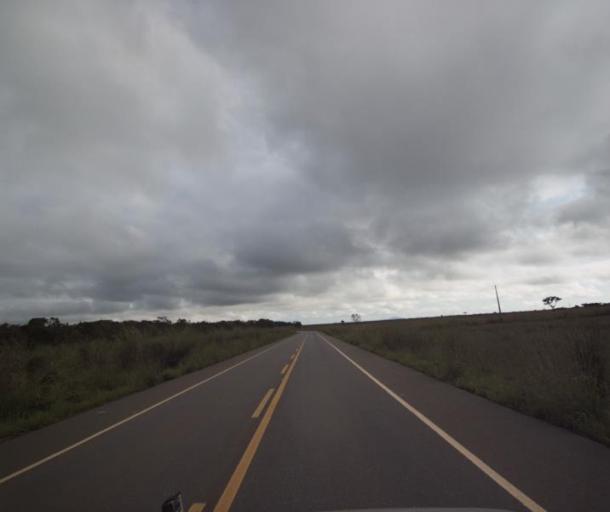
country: BR
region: Goias
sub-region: Padre Bernardo
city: Padre Bernardo
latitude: -15.3394
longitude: -48.6476
